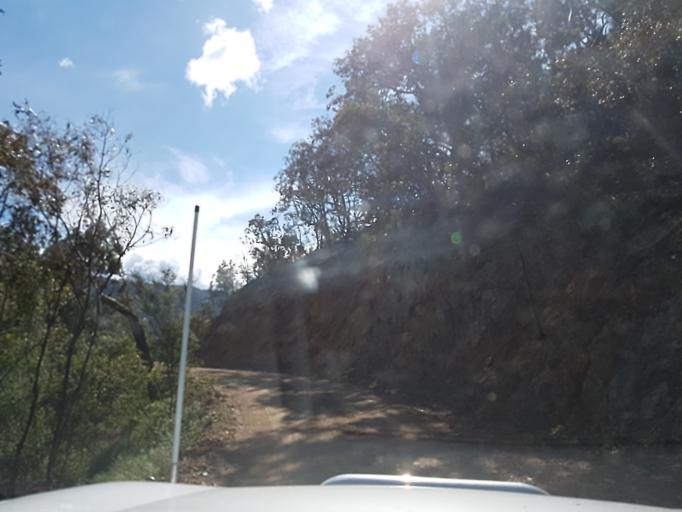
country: AU
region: Victoria
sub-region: Alpine
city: Mount Beauty
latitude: -37.3759
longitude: 147.0403
